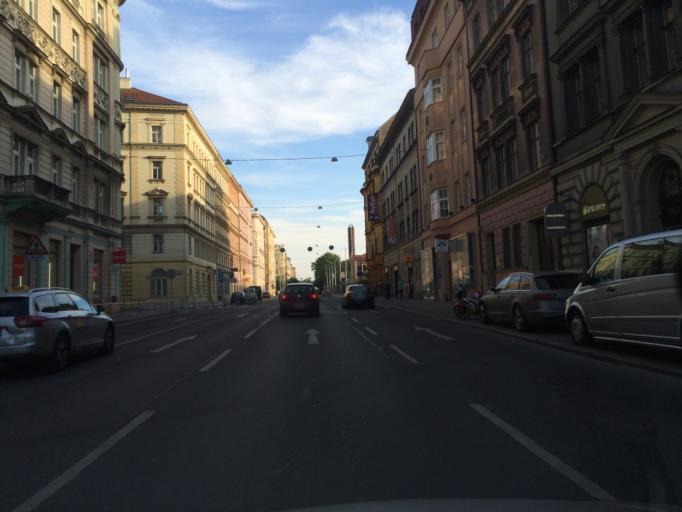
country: CZ
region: Praha
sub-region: Praha 2
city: Vysehrad
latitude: 50.0740
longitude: 14.4291
